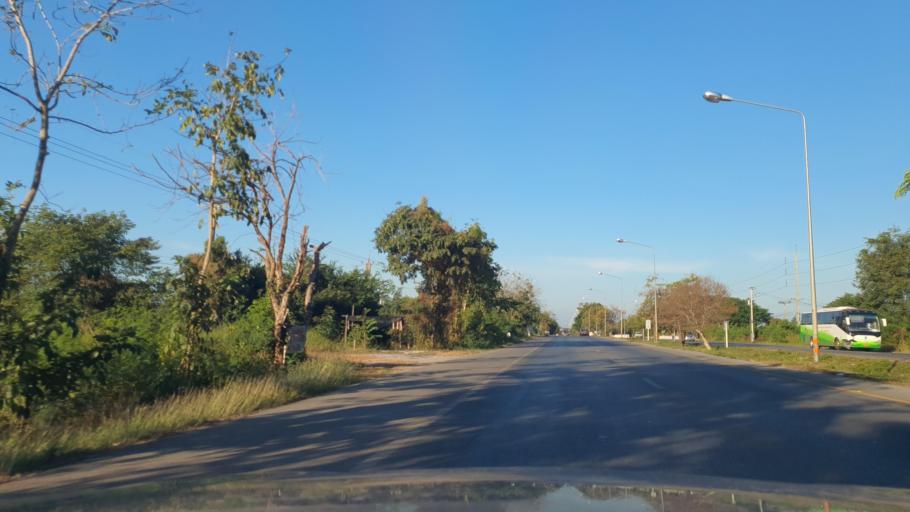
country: TH
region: Phitsanulok
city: Phitsanulok
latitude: 16.8650
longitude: 100.2301
